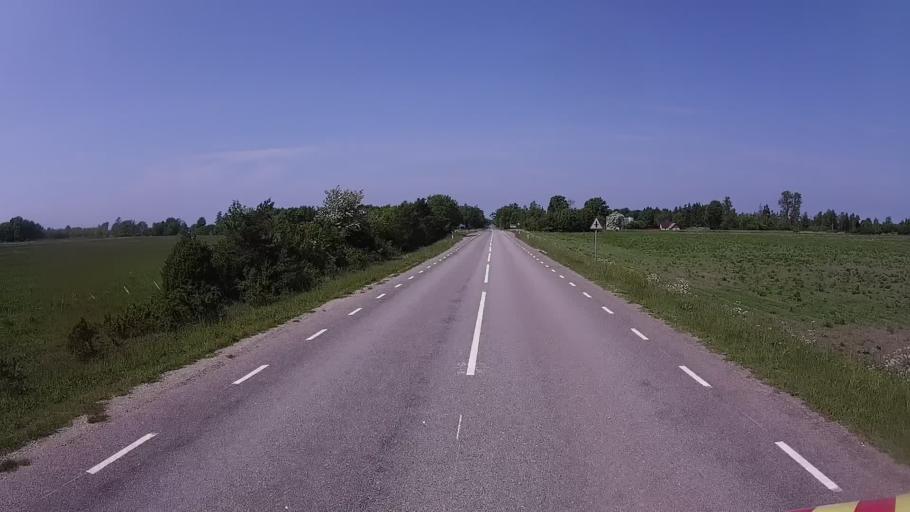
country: EE
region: Saare
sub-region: Kuressaare linn
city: Kuressaare
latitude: 58.3626
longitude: 22.0584
